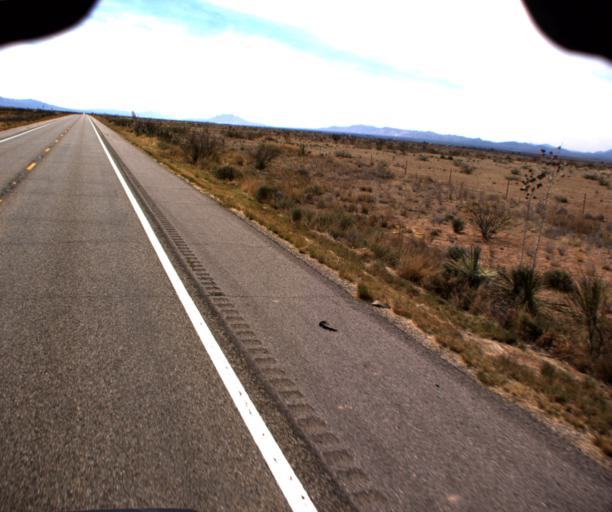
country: US
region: Arizona
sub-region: Cochise County
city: Pirtleville
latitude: 31.4904
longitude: -109.6297
